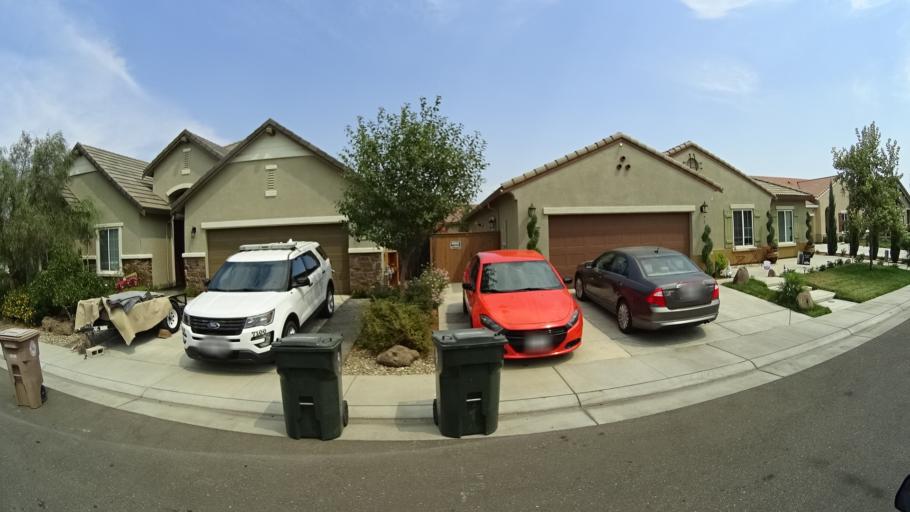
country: US
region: California
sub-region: Sacramento County
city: Laguna
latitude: 38.3928
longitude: -121.4130
